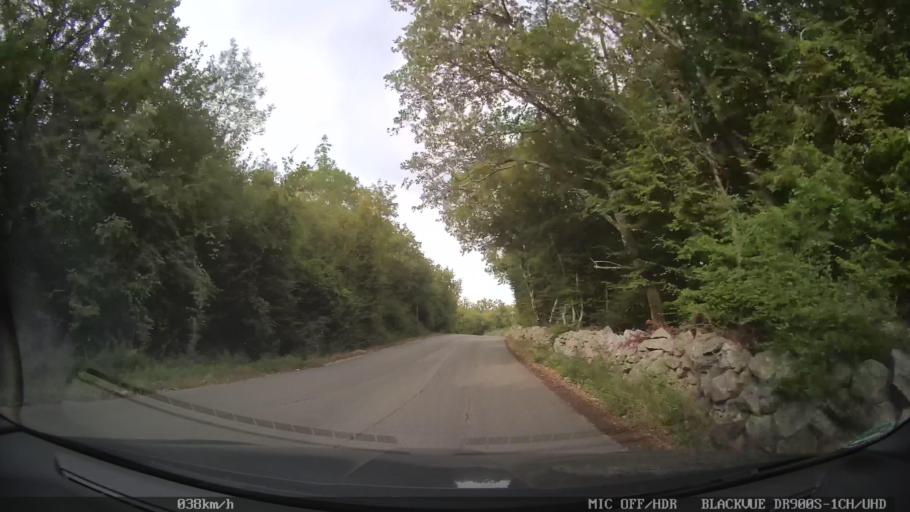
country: HR
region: Primorsko-Goranska
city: Njivice
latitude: 45.0884
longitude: 14.4415
